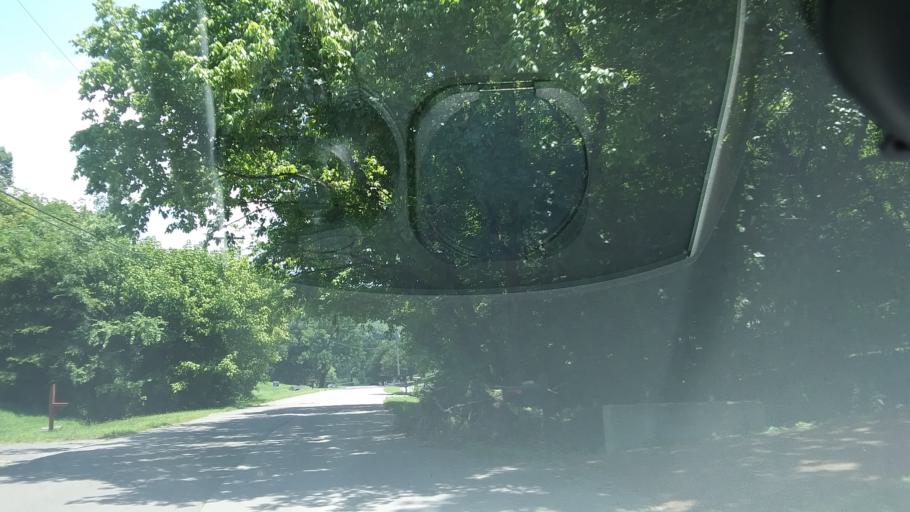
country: US
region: Tennessee
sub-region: Davidson County
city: Belle Meade
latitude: 36.1262
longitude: -86.9371
